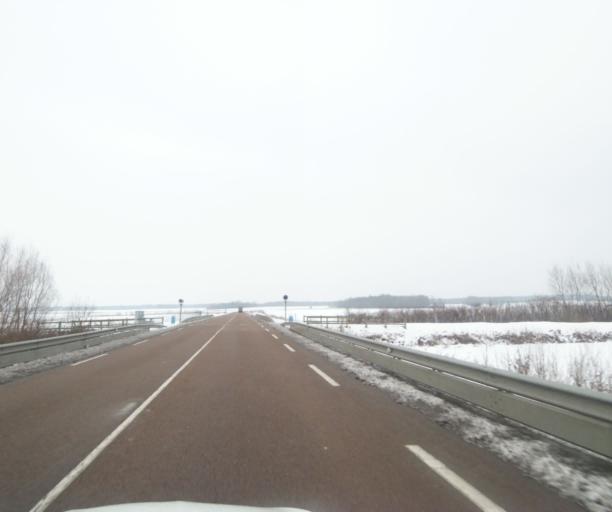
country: FR
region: Champagne-Ardenne
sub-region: Departement de la Haute-Marne
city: Saint-Dizier
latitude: 48.5905
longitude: 4.8910
